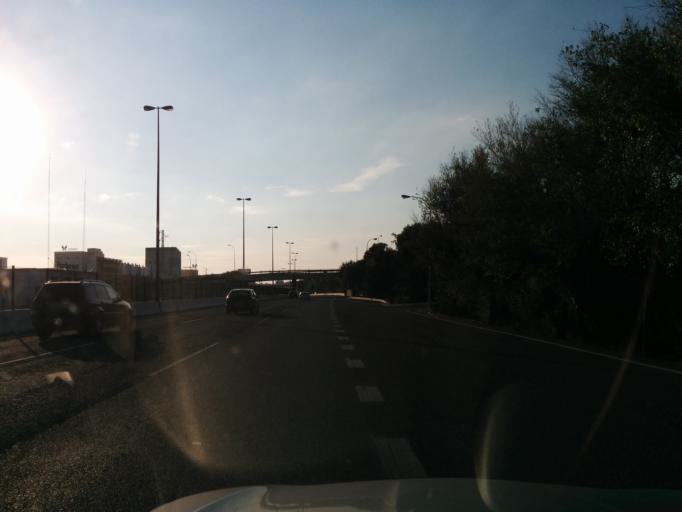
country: ES
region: Andalusia
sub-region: Provincia de Sevilla
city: Sevilla
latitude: 37.3861
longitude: -5.9215
